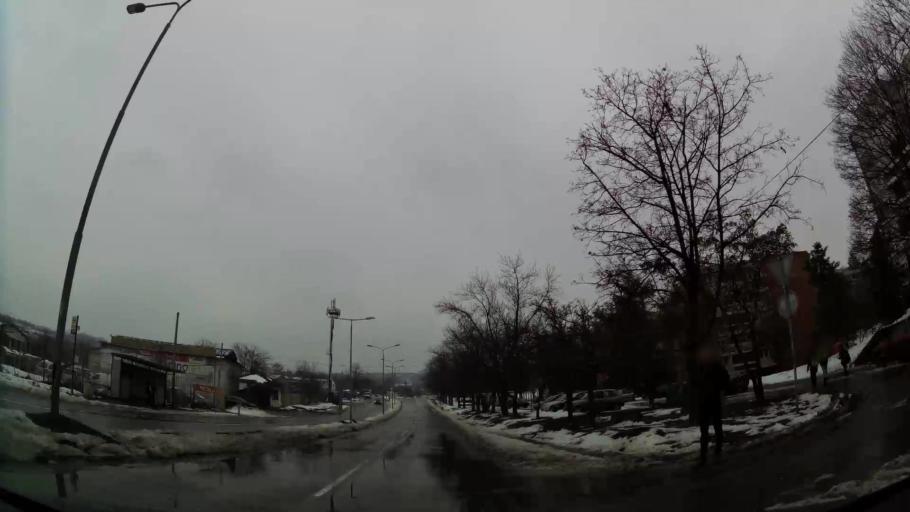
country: RS
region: Central Serbia
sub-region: Belgrade
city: Vozdovac
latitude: 44.7523
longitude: 20.5021
